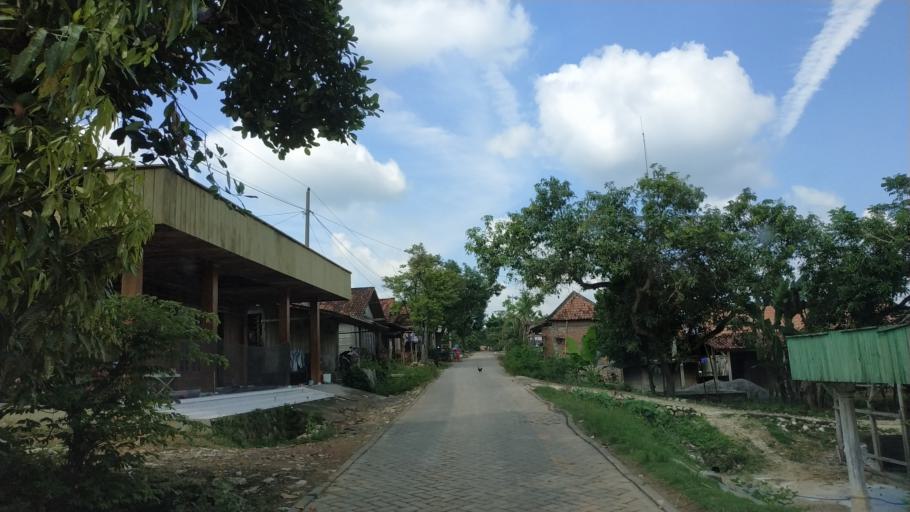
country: ID
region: Central Java
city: Guyangan
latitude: -7.0051
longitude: 111.1112
